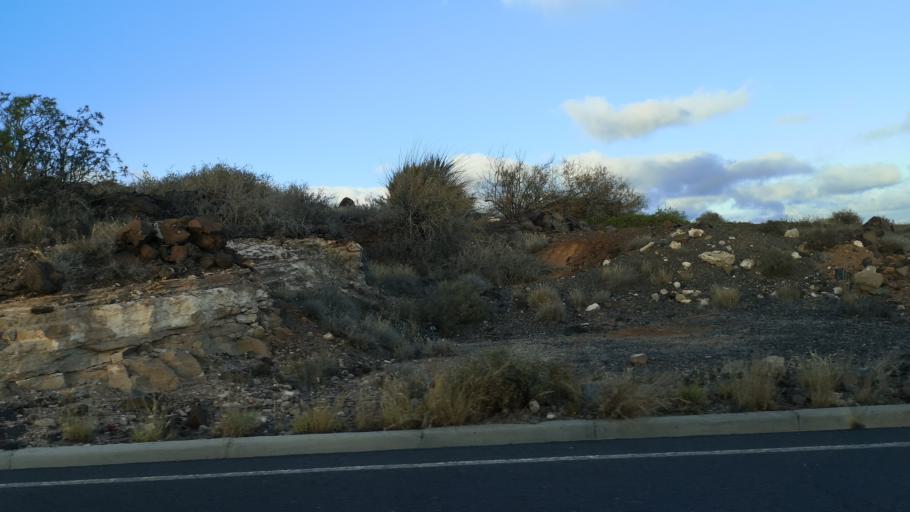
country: ES
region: Canary Islands
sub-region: Provincia de Santa Cruz de Tenerife
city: Alajero
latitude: 28.0329
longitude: -17.2197
